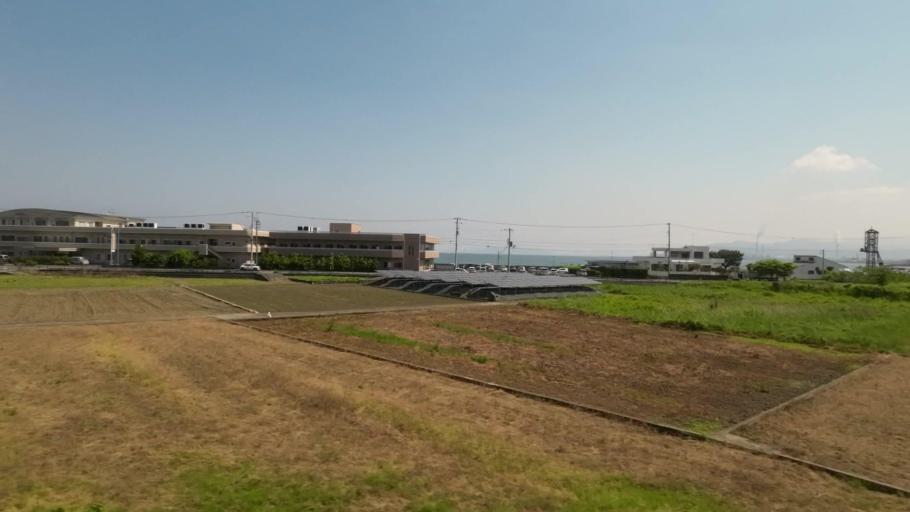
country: JP
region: Ehime
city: Kawanoecho
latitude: 33.9685
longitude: 133.4876
